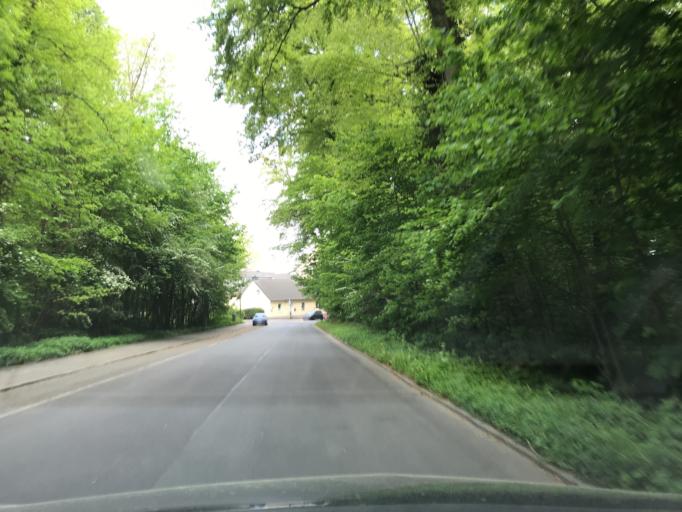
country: DE
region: North Rhine-Westphalia
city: Witten
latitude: 51.4827
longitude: 7.3694
